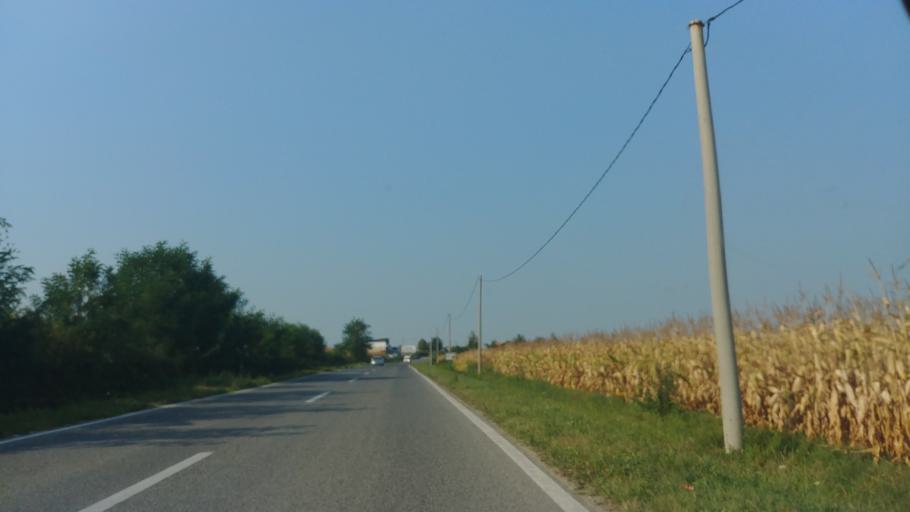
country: BA
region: Brcko
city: Brcko
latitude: 44.7734
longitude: 18.8095
